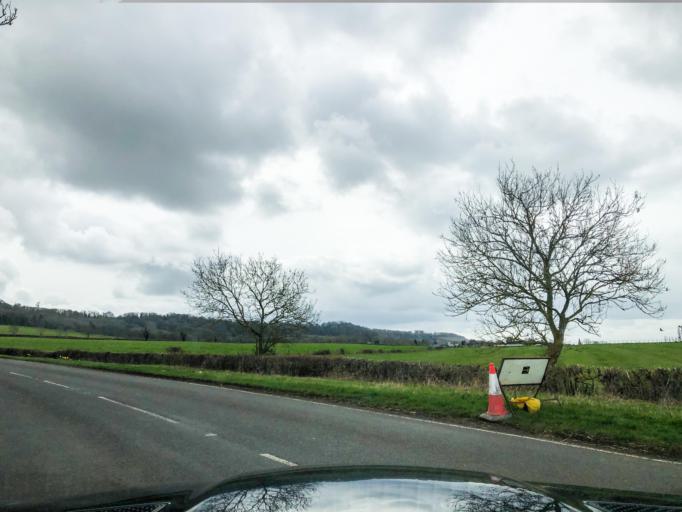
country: GB
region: England
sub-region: Oxfordshire
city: Hanwell
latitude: 52.1387
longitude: -1.4509
